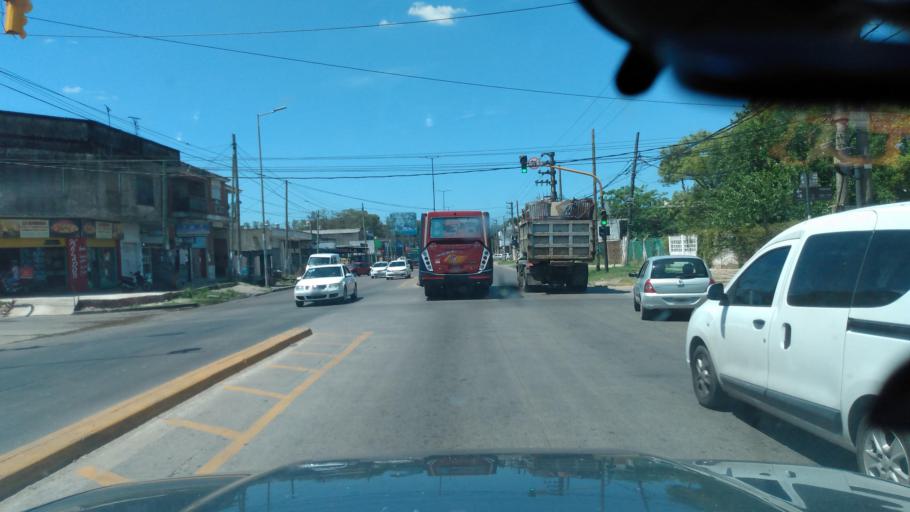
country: AR
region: Buenos Aires
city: Hurlingham
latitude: -34.5625
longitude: -58.7350
